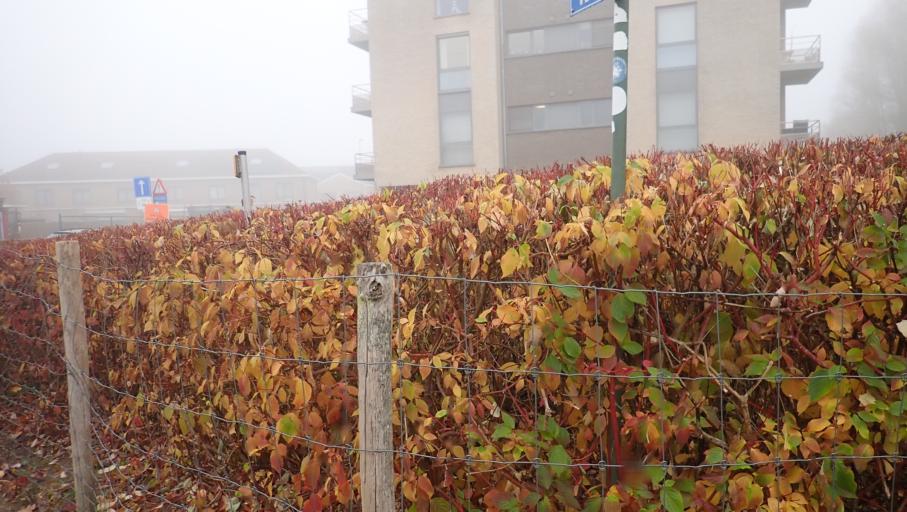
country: BE
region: Flanders
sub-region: Provincie Oost-Vlaanderen
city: Temse
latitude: 51.1311
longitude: 4.2046
